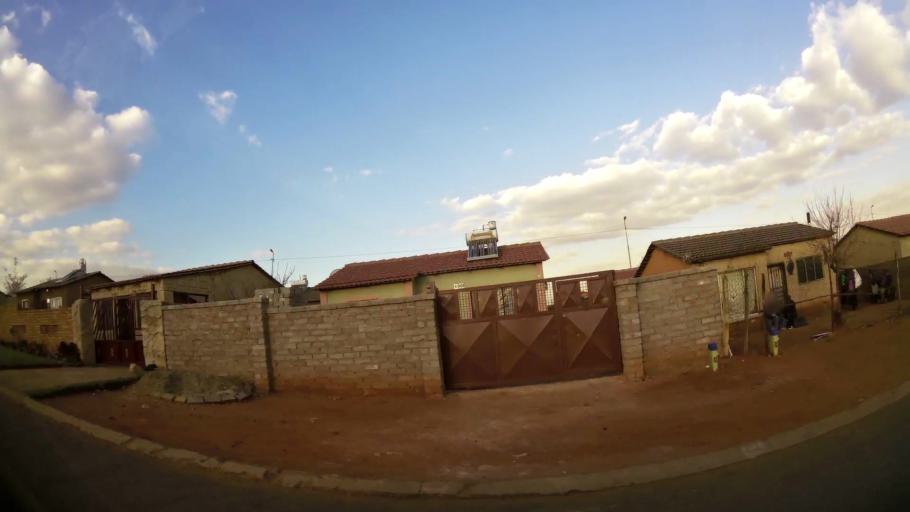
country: ZA
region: Gauteng
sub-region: West Rand District Municipality
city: Krugersdorp
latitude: -26.0784
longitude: 27.7593
